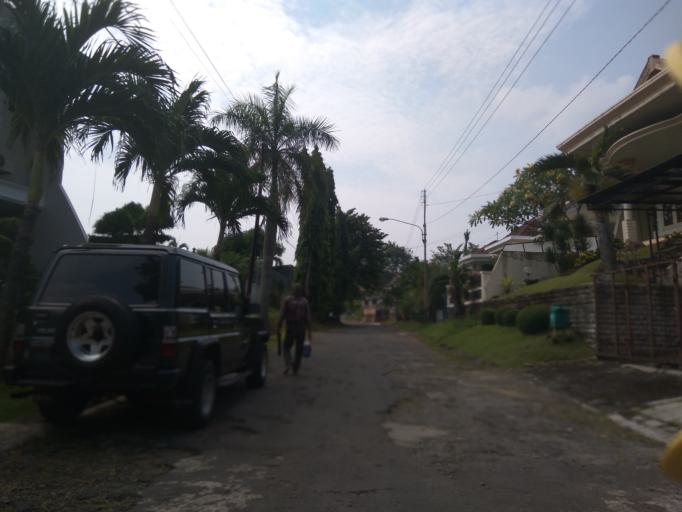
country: ID
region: Central Java
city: Semarang
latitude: -7.0456
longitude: 110.4147
